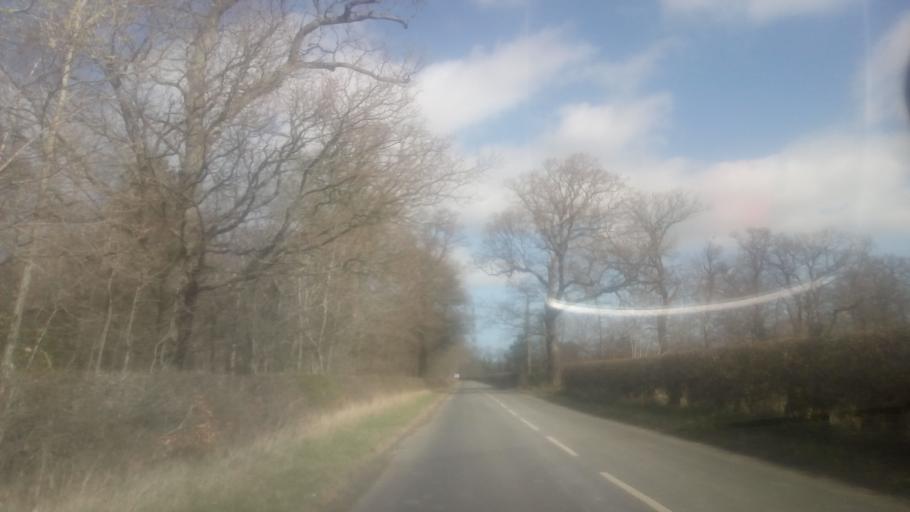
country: GB
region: Scotland
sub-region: Fife
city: Pathhead
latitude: 55.8899
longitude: -2.9568
